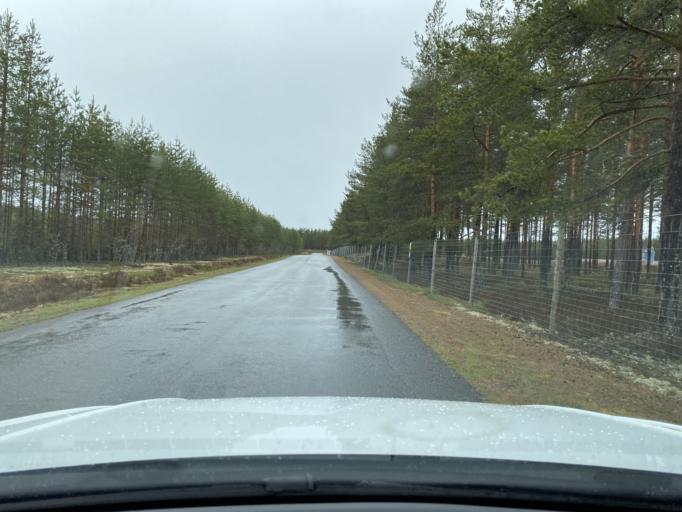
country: FI
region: Satakunta
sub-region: Pori
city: Vampula
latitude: 60.9723
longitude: 22.6654
